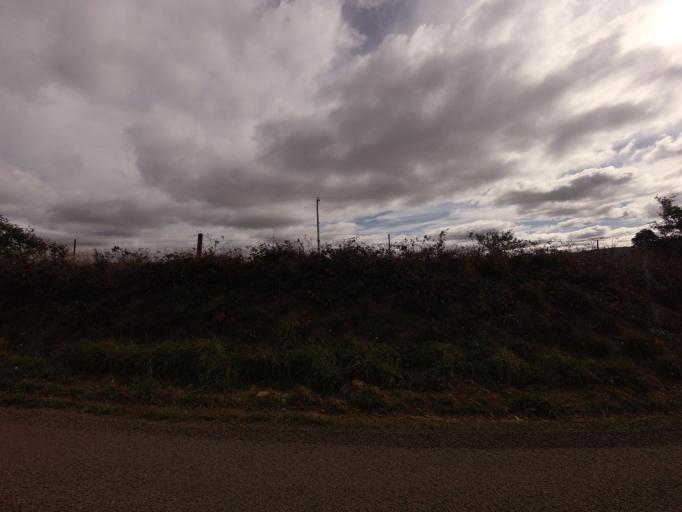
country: AU
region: Tasmania
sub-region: Brighton
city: Bridgewater
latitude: -42.4315
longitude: 147.3863
